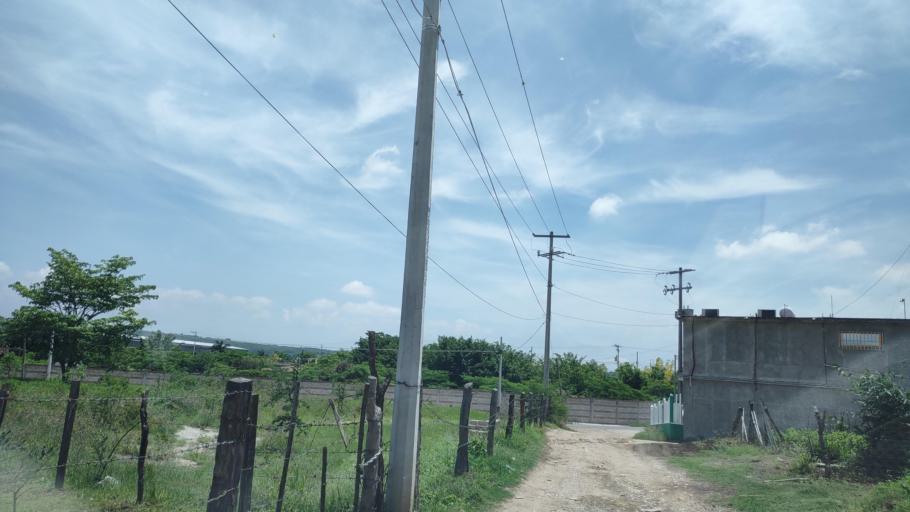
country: MX
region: Veracruz
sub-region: Emiliano Zapata
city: Dos Rios
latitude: 19.4287
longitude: -96.8008
